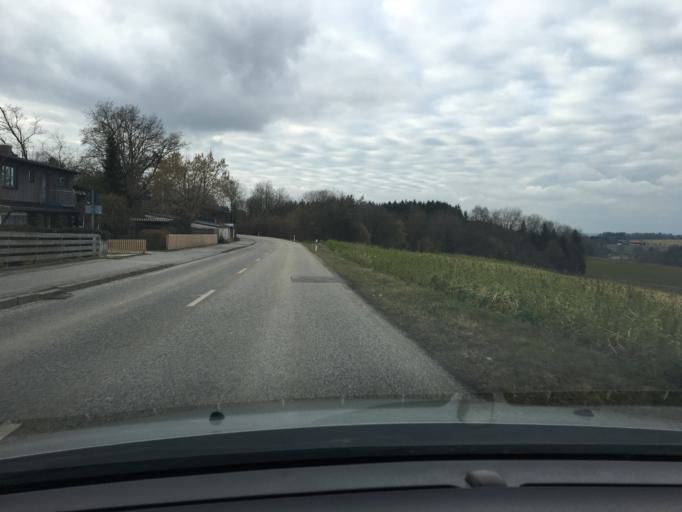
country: DE
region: Bavaria
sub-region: Lower Bavaria
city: Kumhausen
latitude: 48.4926
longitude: 12.1840
